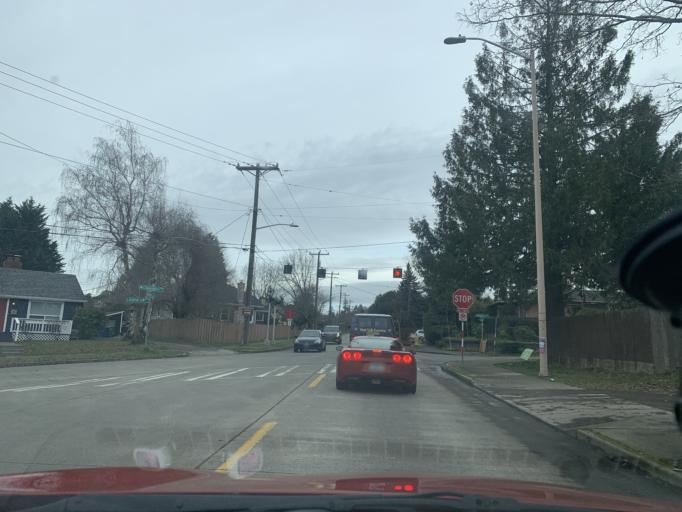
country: US
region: Washington
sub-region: King County
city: Bryn Mawr-Skyway
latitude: 47.5282
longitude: -122.2663
